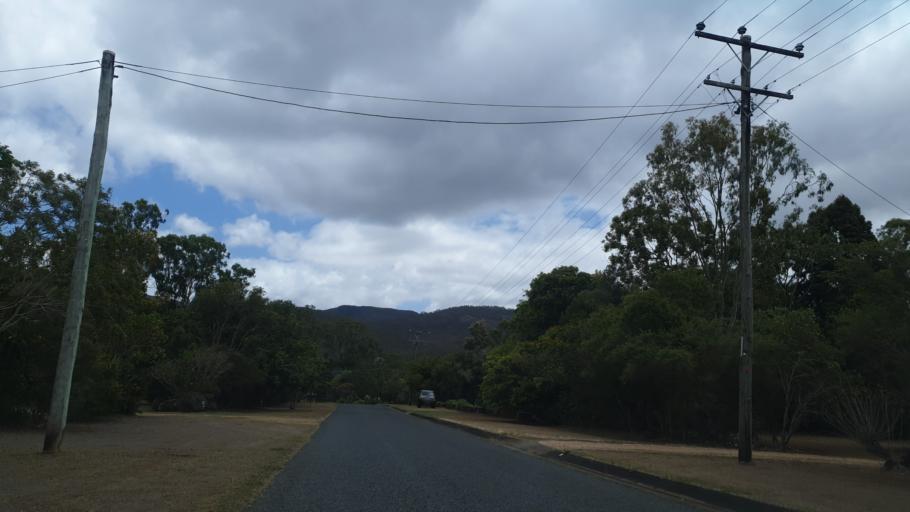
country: AU
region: Queensland
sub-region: Tablelands
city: Tolga
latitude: -17.2073
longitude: 145.4398
